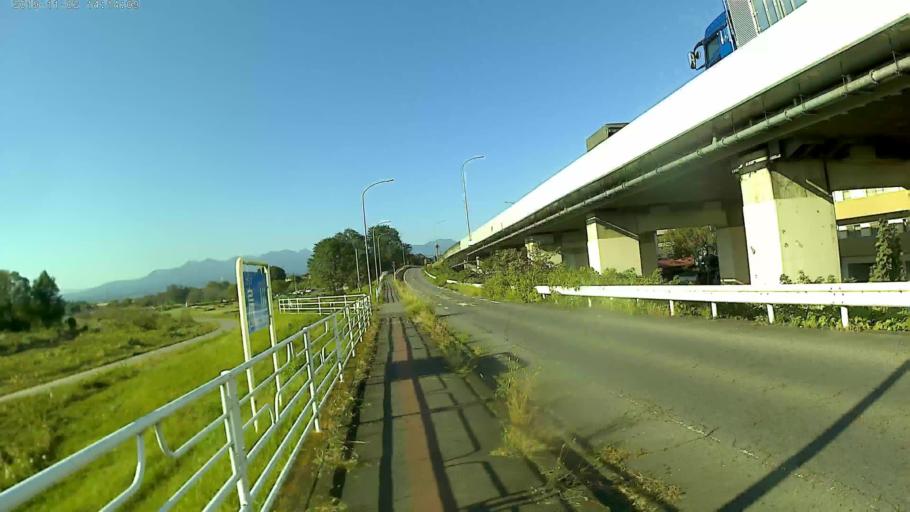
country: JP
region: Gunma
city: Takasaki
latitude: 36.3339
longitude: 138.9910
